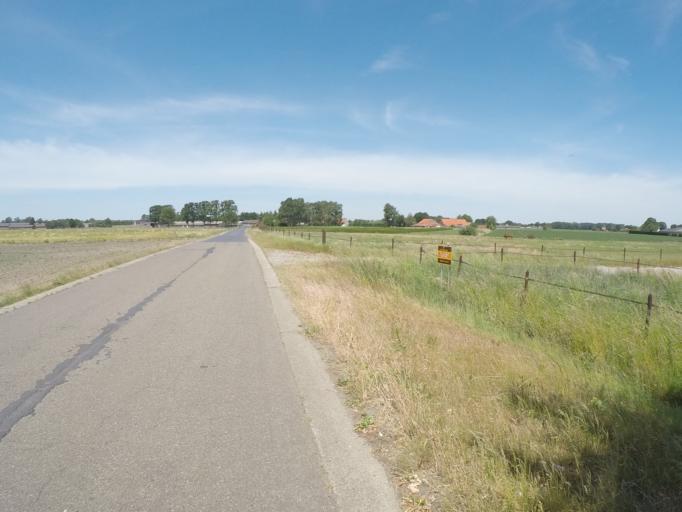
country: BE
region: Flanders
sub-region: Provincie Antwerpen
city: Brecht
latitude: 51.3803
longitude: 4.6566
